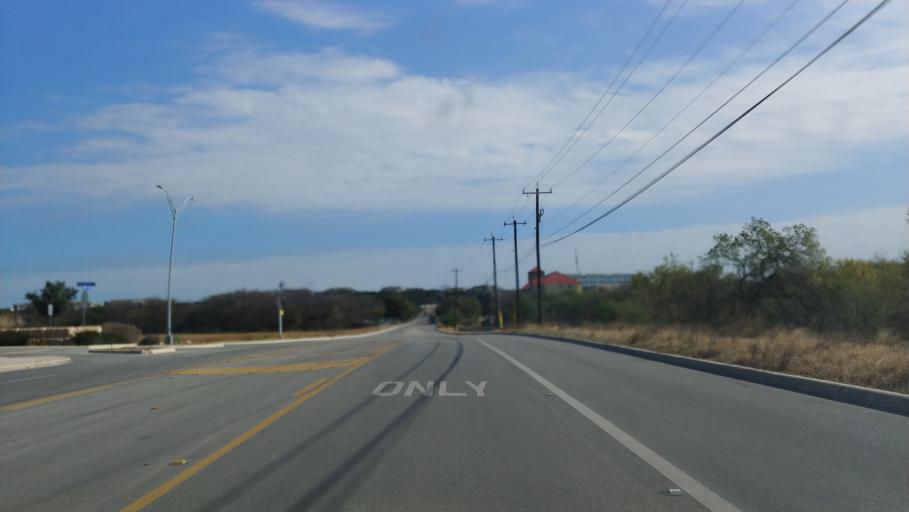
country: US
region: Texas
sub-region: Bexar County
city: Shavano Park
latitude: 29.5792
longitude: -98.6024
